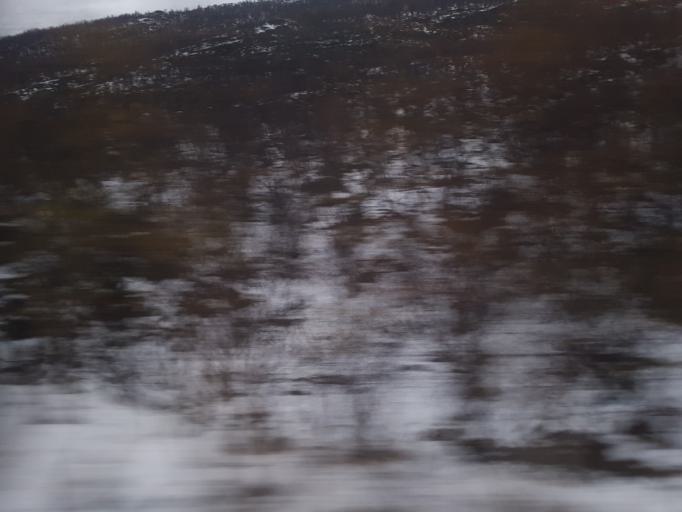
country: NO
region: Sor-Trondelag
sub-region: Oppdal
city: Oppdal
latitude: 62.3453
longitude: 9.6259
